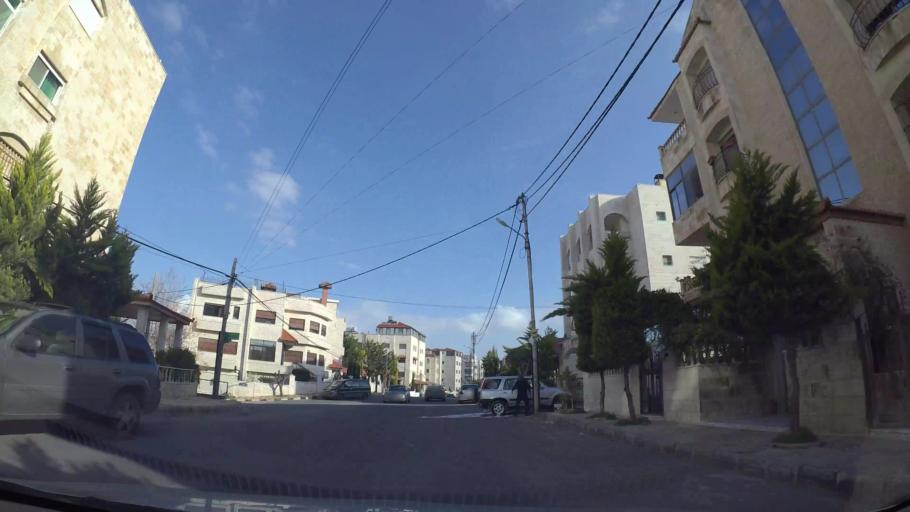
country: JO
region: Amman
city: Al Jubayhah
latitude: 32.0129
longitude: 35.8617
